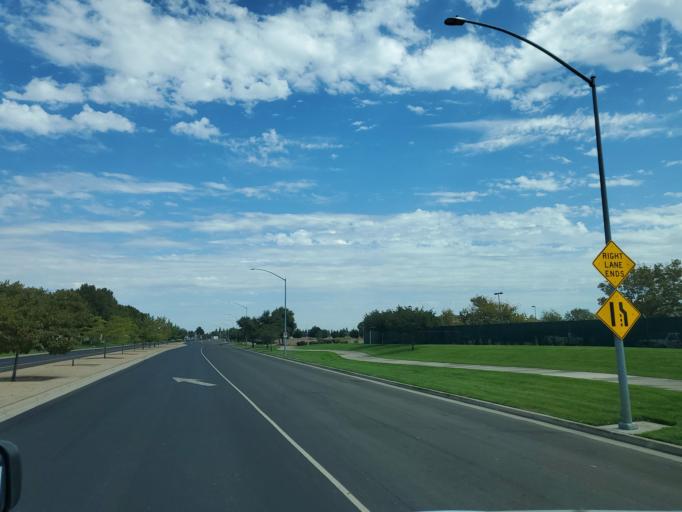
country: US
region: California
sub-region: San Joaquin County
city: Kennedy
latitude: 37.9060
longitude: -121.2418
